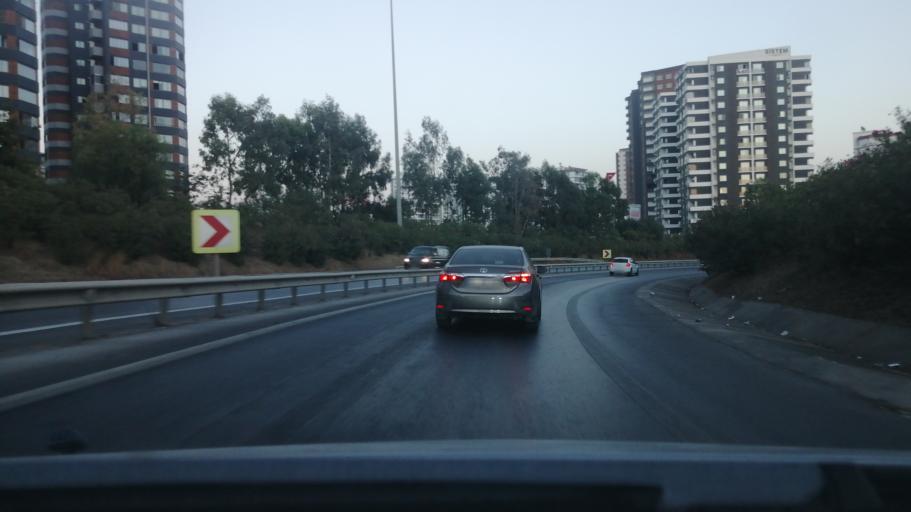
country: TR
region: Adana
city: Seyhan
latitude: 37.0344
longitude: 35.2514
